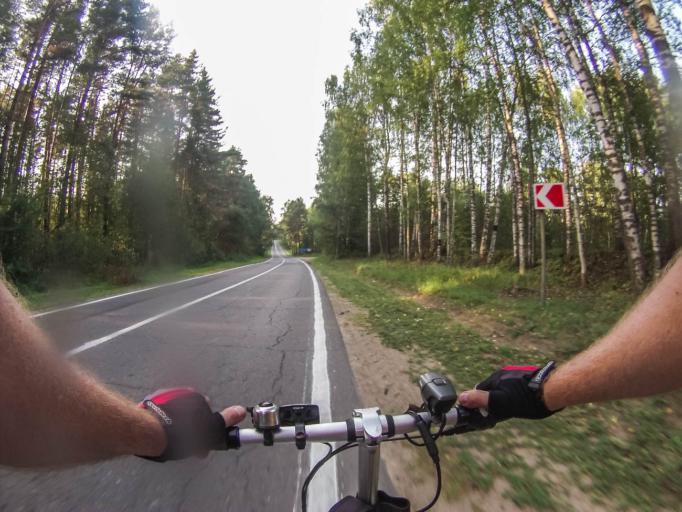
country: RU
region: Jaroslavl
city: Myshkin
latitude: 57.7605
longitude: 38.4462
